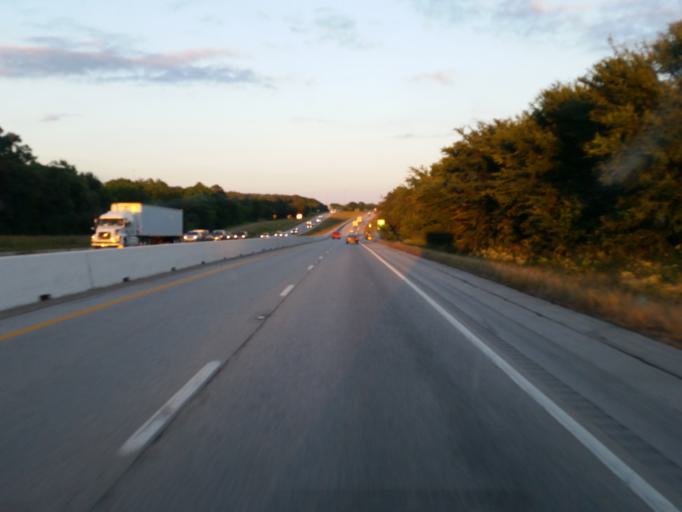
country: US
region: Texas
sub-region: Smith County
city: Hideaway
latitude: 32.4887
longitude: -95.5448
